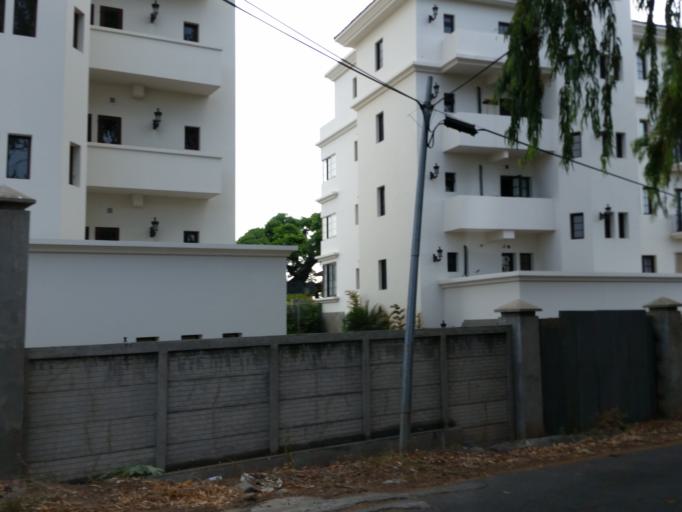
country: NI
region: Managua
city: Managua
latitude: 12.0962
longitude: -86.2460
